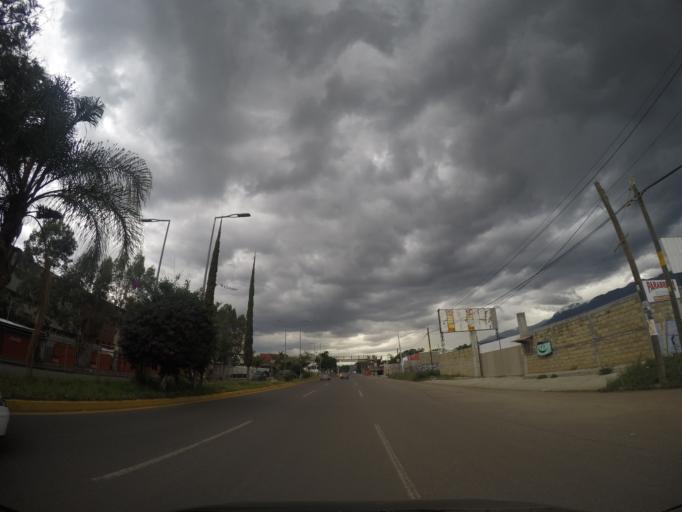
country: MX
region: Oaxaca
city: Tlalixtac de Cabrera
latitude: 17.0550
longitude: -96.6527
